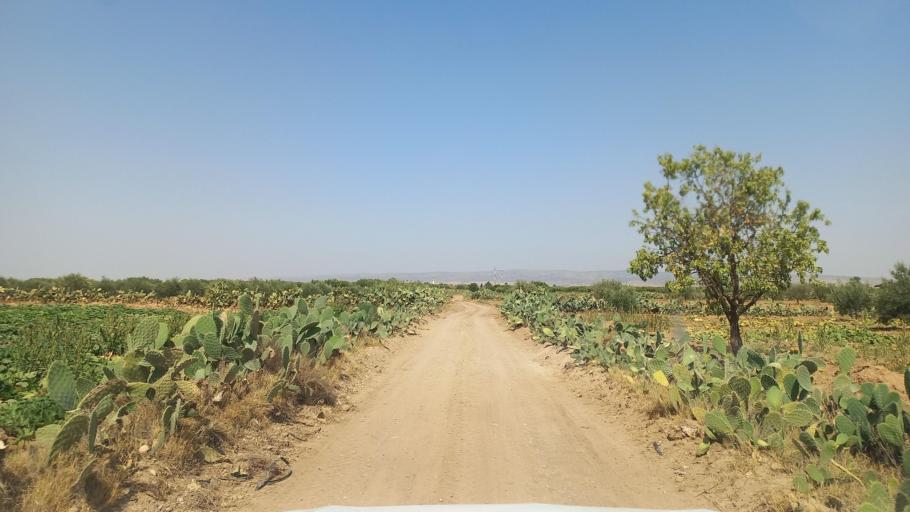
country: TN
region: Al Qasrayn
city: Kasserine
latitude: 35.2468
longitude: 9.0382
